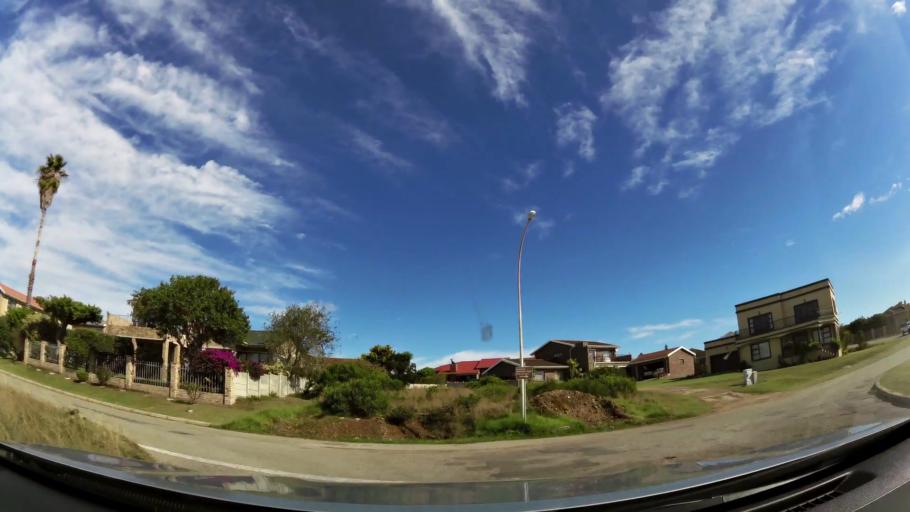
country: ZA
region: Eastern Cape
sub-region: Cacadu District Municipality
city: Jeffrey's Bay
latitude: -34.0146
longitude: 24.9228
